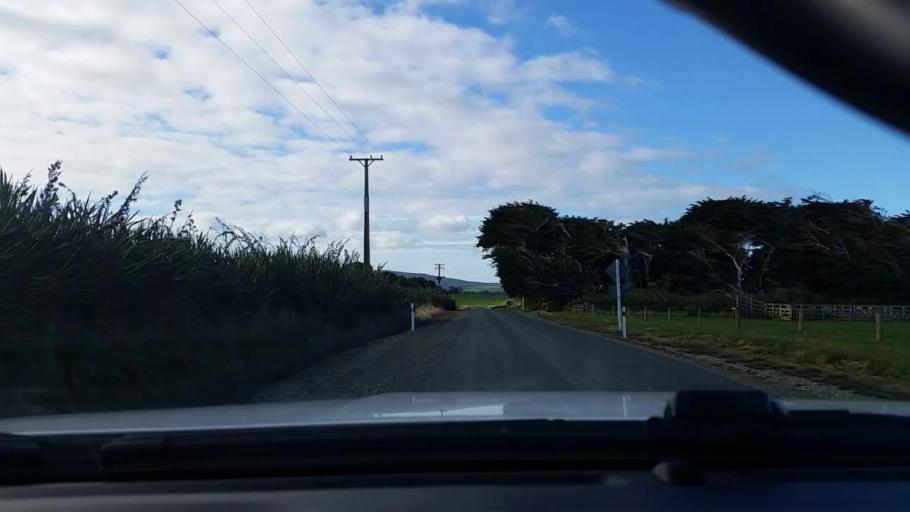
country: NZ
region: Southland
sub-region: Southland District
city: Riverton
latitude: -46.3303
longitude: 167.7141
